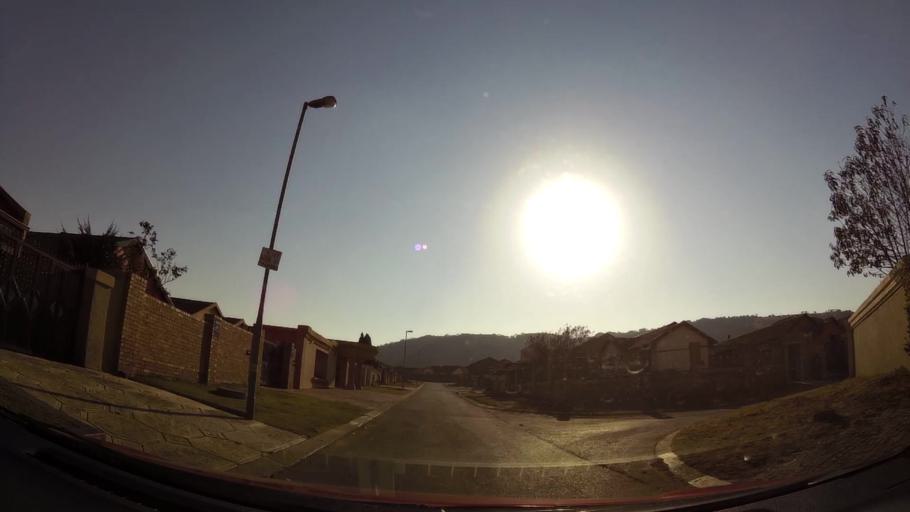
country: ZA
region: Gauteng
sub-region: City of Johannesburg Metropolitan Municipality
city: Soweto
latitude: -26.2954
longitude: 27.9600
